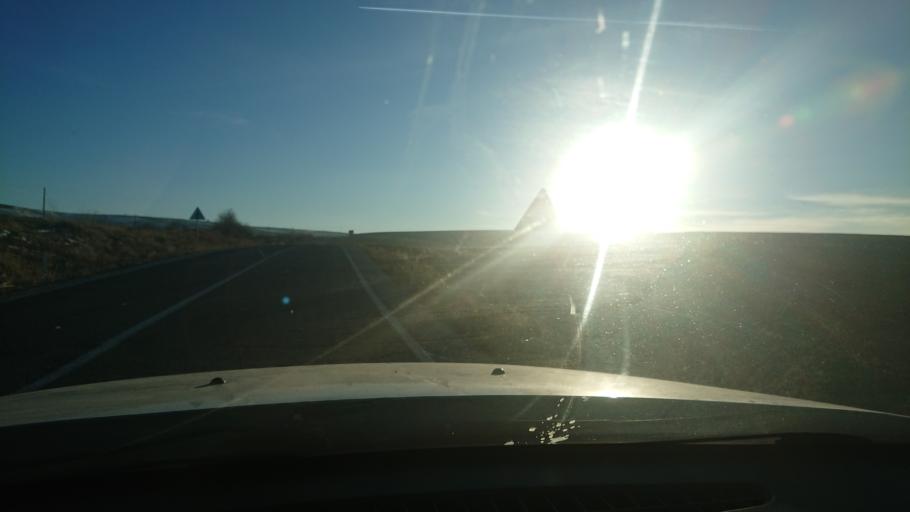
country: TR
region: Aksaray
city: Agacoren
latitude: 38.8536
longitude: 33.9006
